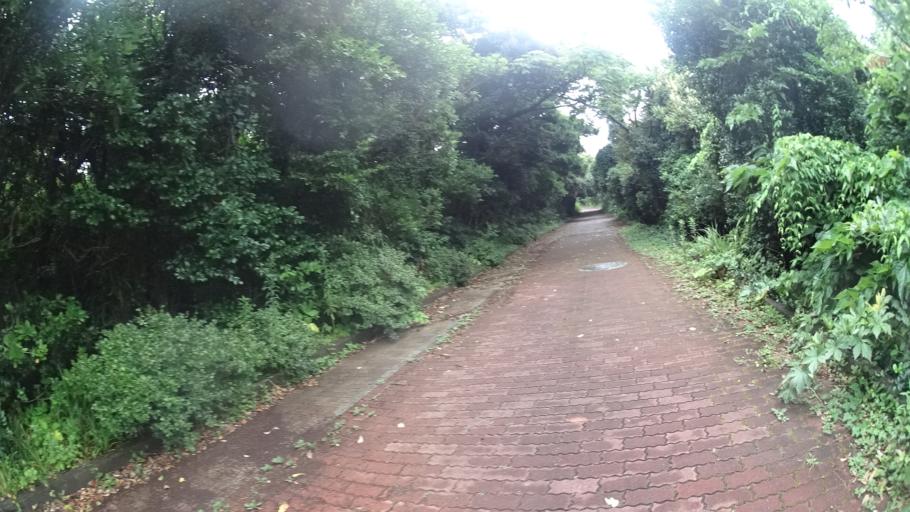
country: JP
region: Shizuoka
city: Shimoda
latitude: 34.3210
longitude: 139.2154
